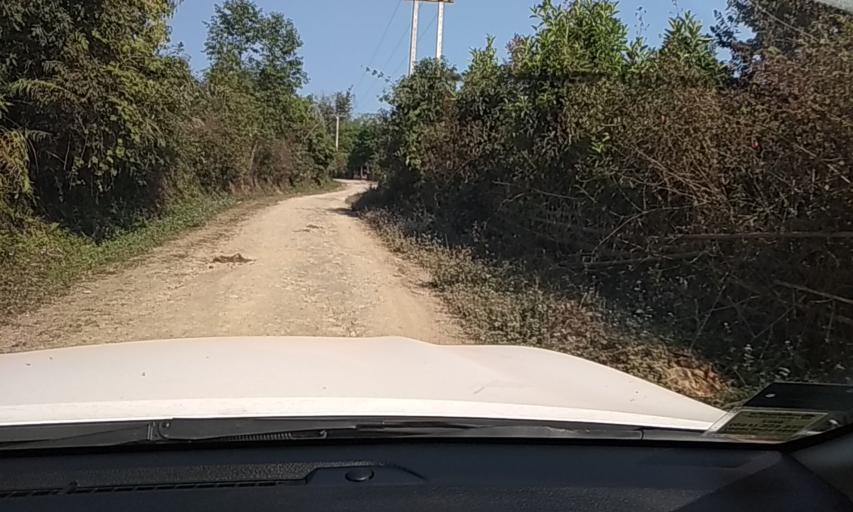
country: LA
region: Phongsali
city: Phongsali
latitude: 21.6974
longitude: 102.0823
